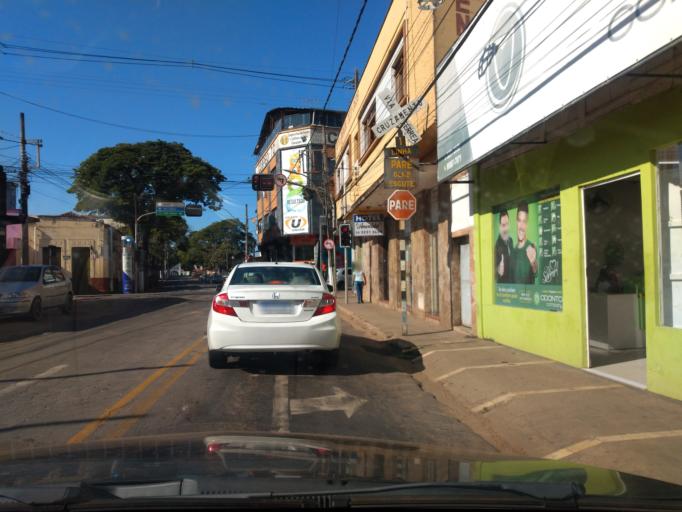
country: BR
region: Minas Gerais
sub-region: Tres Coracoes
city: Tres Coracoes
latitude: -21.6990
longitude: -45.2585
